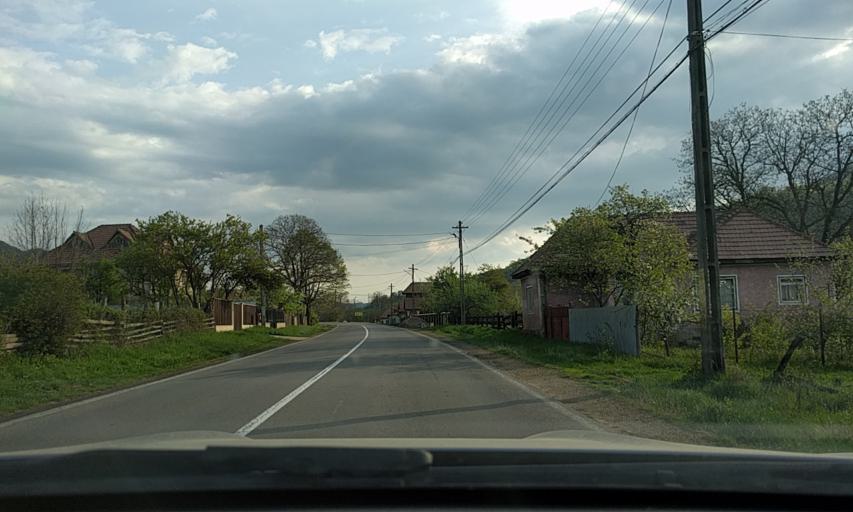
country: RO
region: Bacau
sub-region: Oras Slanic-Moldova
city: Slanic-Moldova
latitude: 46.1473
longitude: 26.4585
